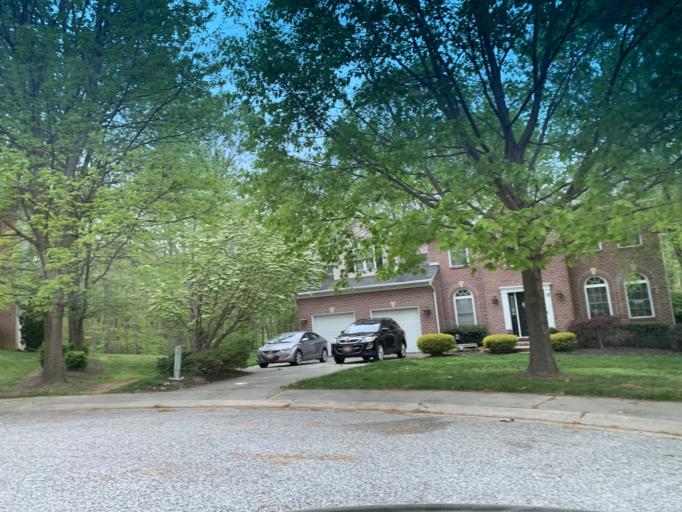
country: US
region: Maryland
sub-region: Harford County
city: South Bel Air
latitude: 39.5265
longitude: -76.3246
